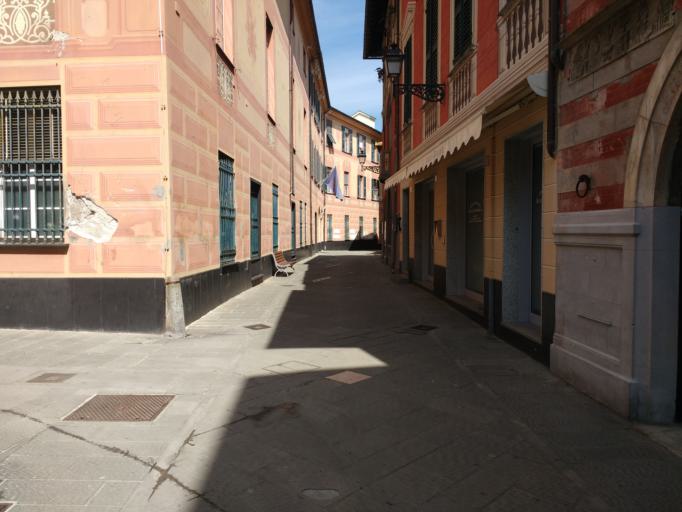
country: IT
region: Liguria
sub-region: Provincia di Genova
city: Rapallo
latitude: 44.3498
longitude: 9.2319
